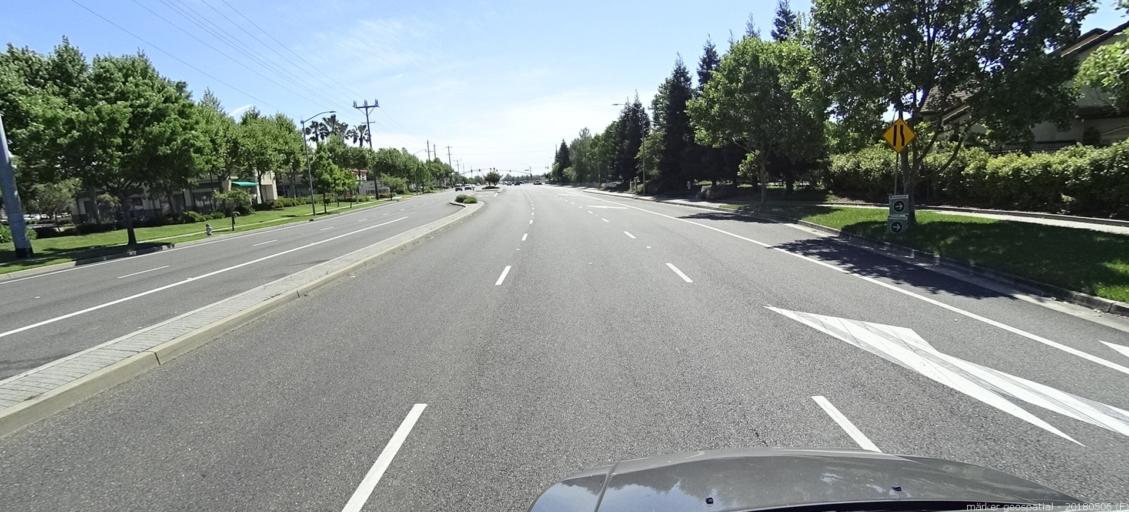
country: US
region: California
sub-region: Sacramento County
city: Laguna
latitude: 38.4380
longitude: -121.4211
